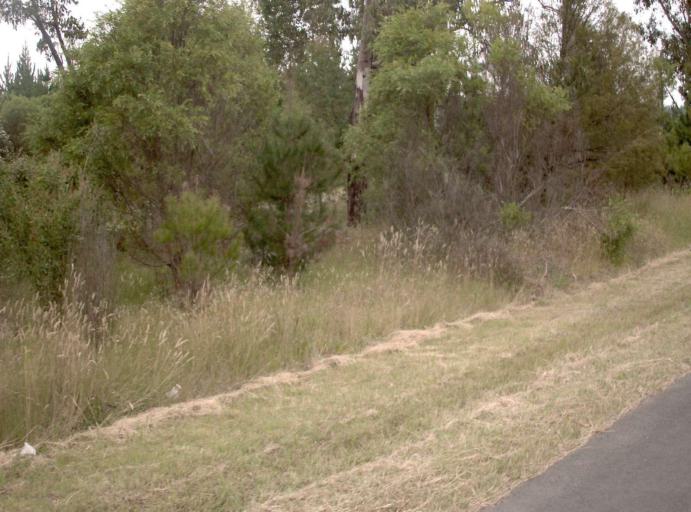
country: AU
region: Victoria
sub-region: Latrobe
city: Moe
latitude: -38.2983
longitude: 146.2847
